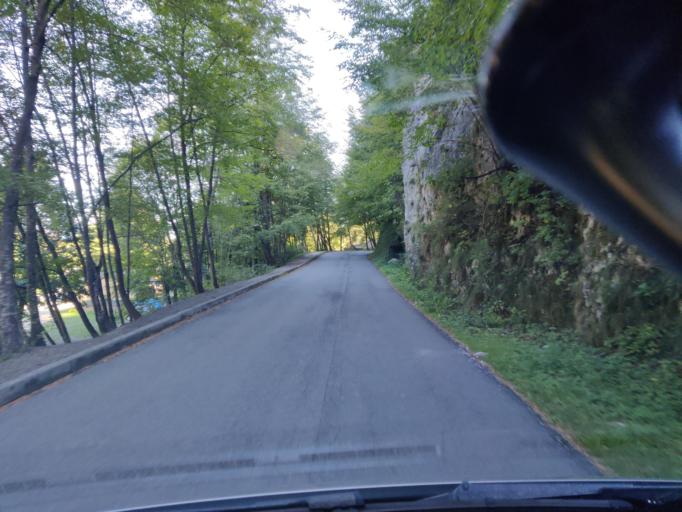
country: IT
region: Lombardy
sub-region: Provincia di Brescia
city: Anfo
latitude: 45.7527
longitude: 10.4946
